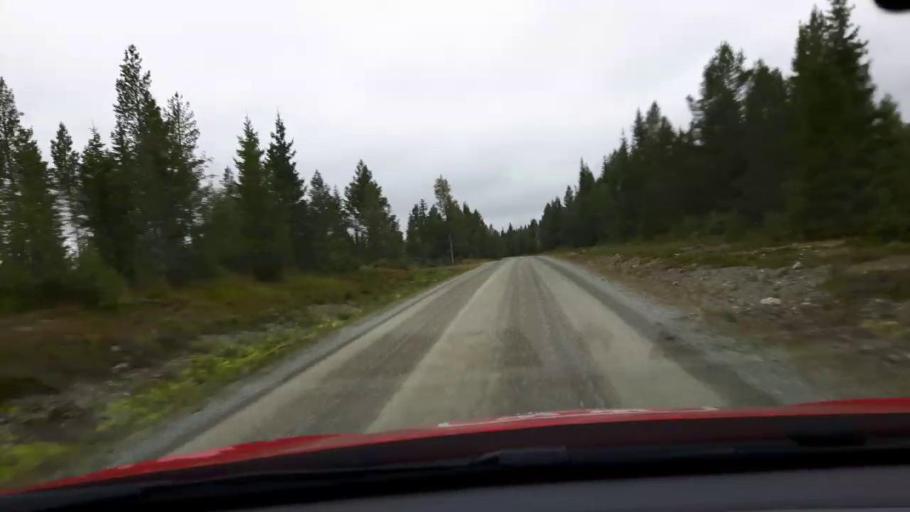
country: SE
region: Jaemtland
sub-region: Bergs Kommun
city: Hoverberg
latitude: 62.8652
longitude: 13.9512
